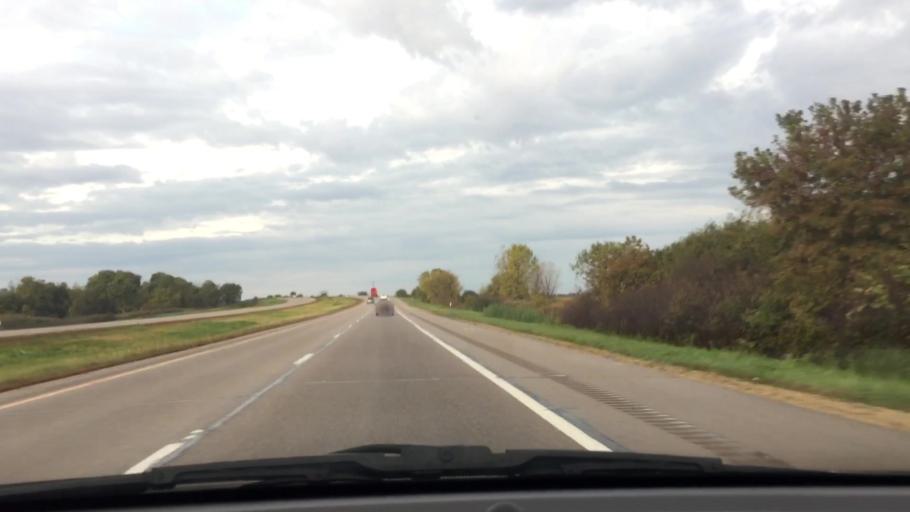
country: US
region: Wisconsin
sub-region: Rock County
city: Clinton
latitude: 42.5791
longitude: -88.7884
